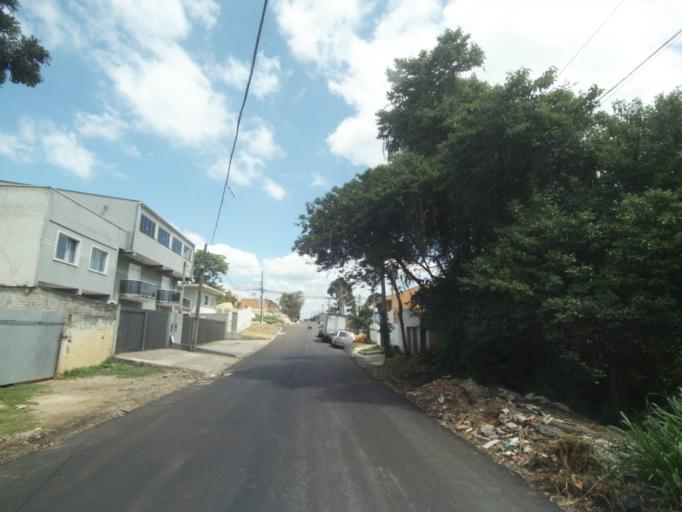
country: BR
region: Parana
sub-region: Curitiba
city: Curitiba
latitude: -25.5089
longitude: -49.3063
